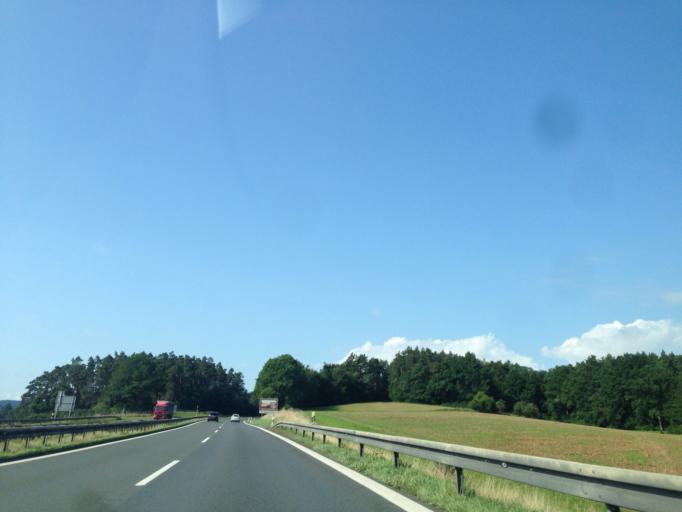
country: DE
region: Bavaria
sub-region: Upper Franconia
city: Neudrossenfeld
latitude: 50.0287
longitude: 11.4564
